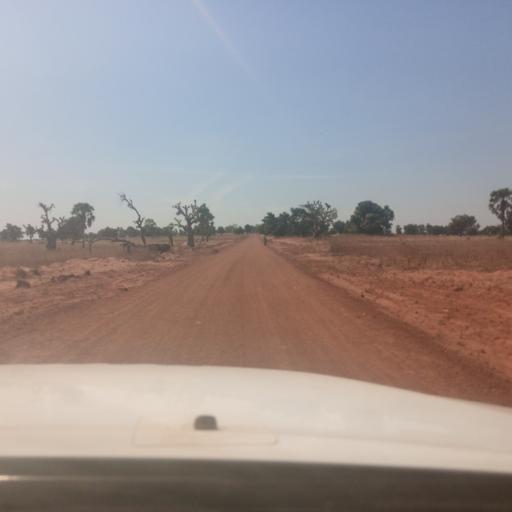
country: NG
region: Adamawa
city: Yola
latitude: 9.1932
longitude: 12.8722
